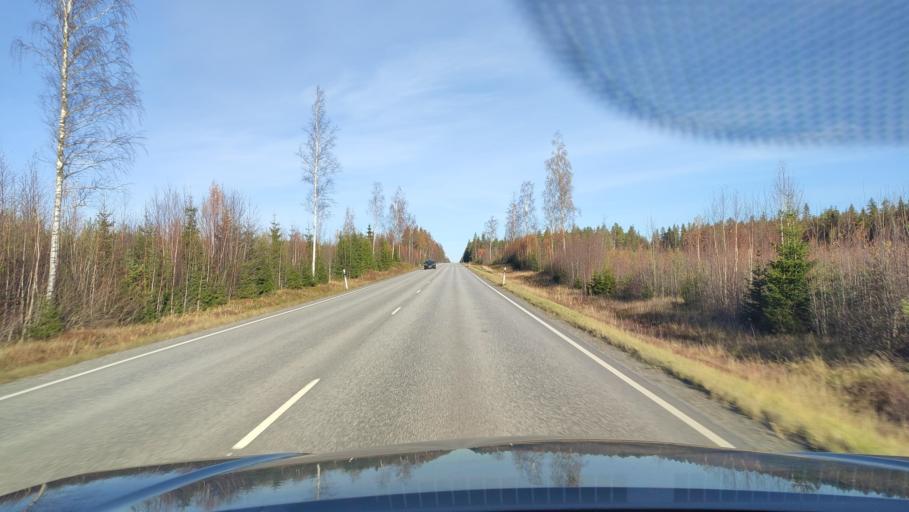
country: FI
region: Ostrobothnia
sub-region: Sydosterbotten
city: Naerpes
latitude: 62.4885
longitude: 21.4431
